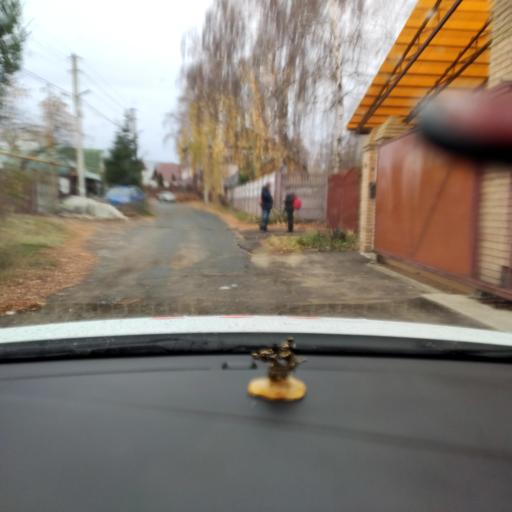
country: RU
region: Tatarstan
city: Vysokaya Gora
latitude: 55.8465
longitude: 49.2384
